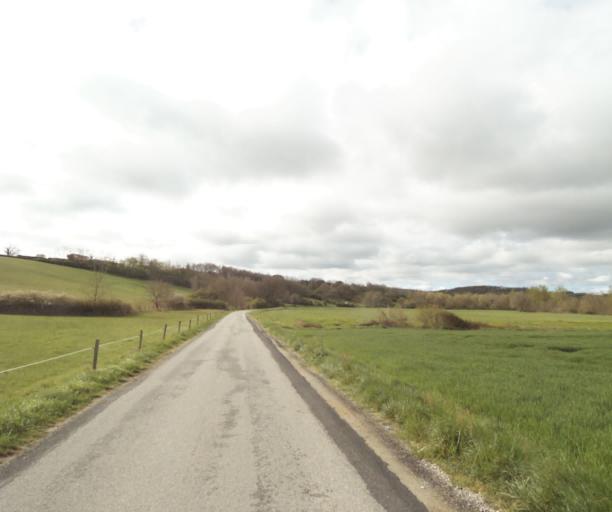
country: FR
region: Midi-Pyrenees
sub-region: Departement de l'Ariege
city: Saverdun
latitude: 43.2321
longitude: 1.5636
